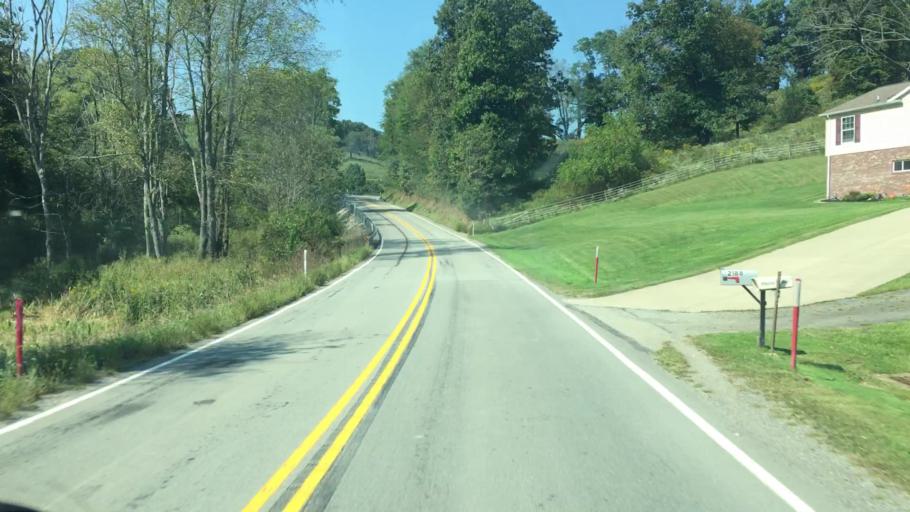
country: US
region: Pennsylvania
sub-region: Greene County
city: Waynesburg
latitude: 39.9817
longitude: -80.3381
